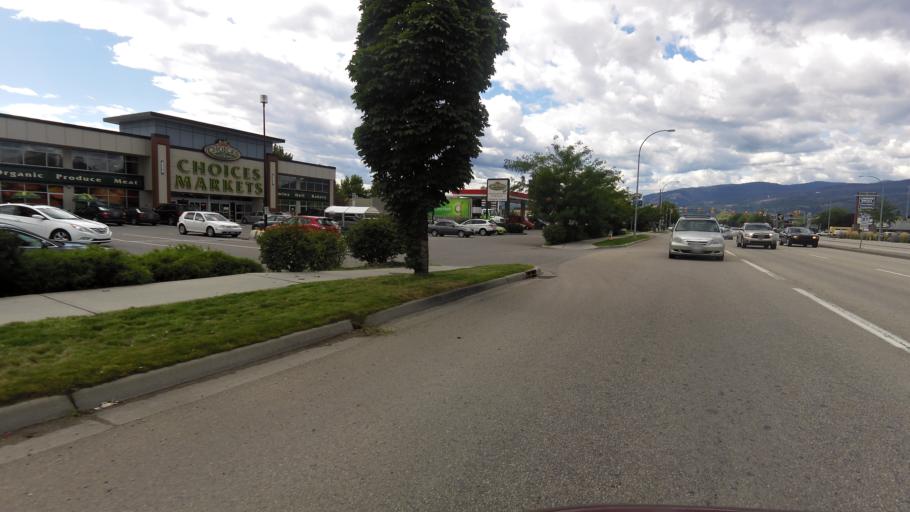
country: CA
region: British Columbia
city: Kelowna
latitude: 49.8818
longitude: -119.4523
